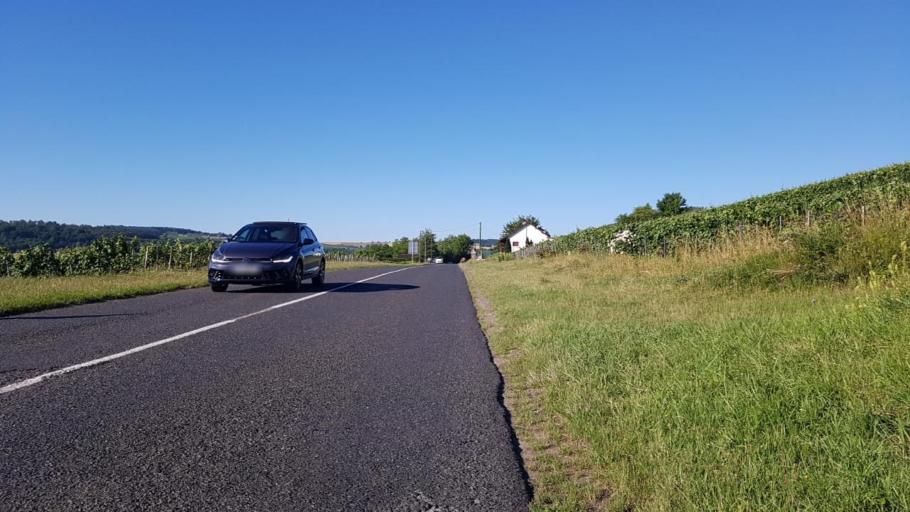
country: FR
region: Picardie
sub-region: Departement de l'Aisne
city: Chezy-sur-Marne
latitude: 49.0051
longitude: 3.3746
